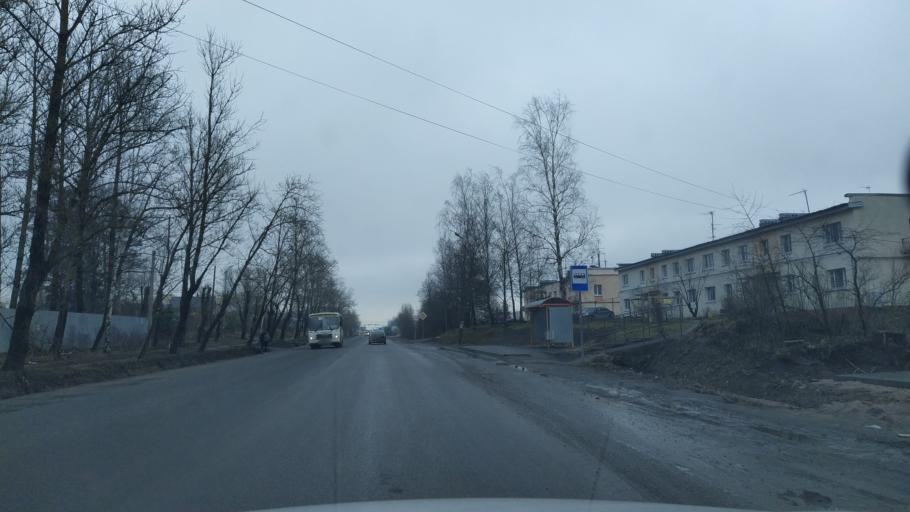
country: RU
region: St.-Petersburg
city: Aleksandrovskaya
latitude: 59.7240
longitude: 30.2561
